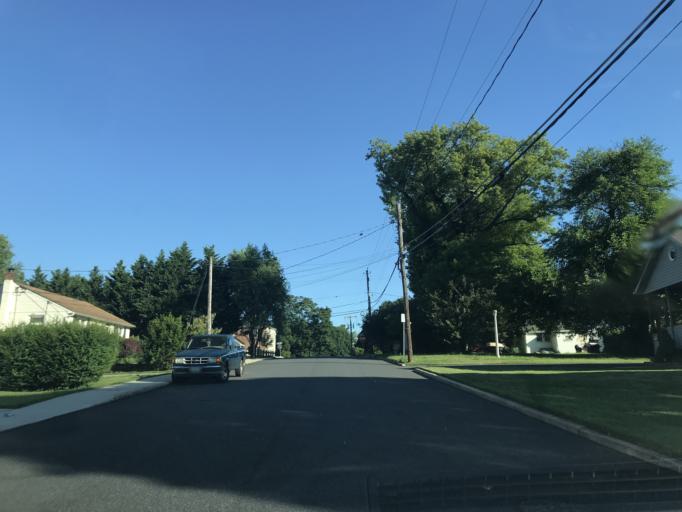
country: US
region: Maryland
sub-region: Harford County
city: Bel Air
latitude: 39.5351
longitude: -76.3433
